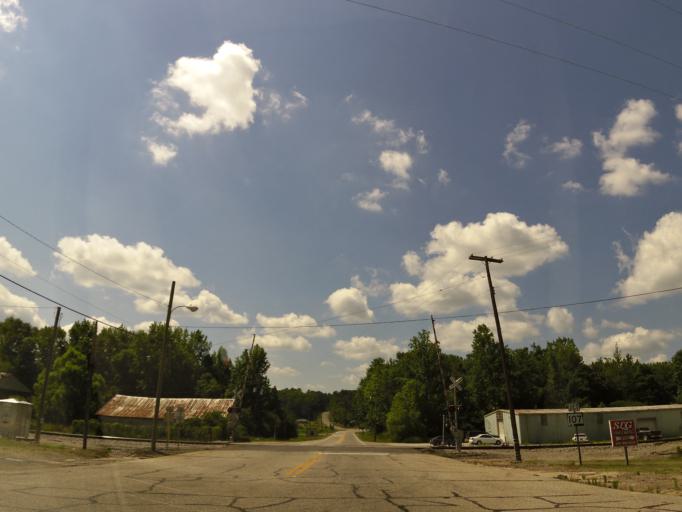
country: US
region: Alabama
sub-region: Marion County
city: Guin
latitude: 33.9645
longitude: -87.9149
